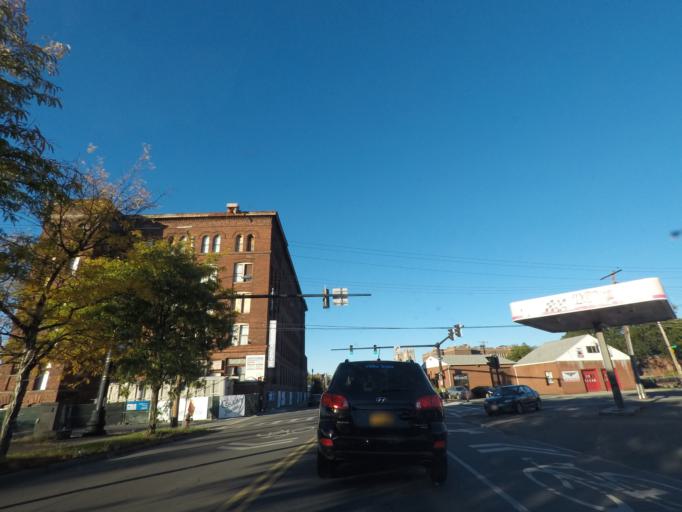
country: US
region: New York
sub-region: Albany County
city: Green Island
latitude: 42.7457
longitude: -73.6838
